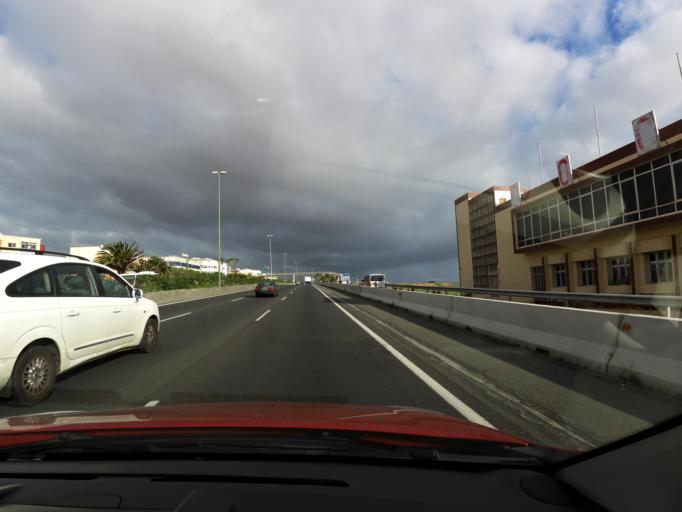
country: ES
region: Canary Islands
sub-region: Provincia de Las Palmas
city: Telde
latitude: 27.9832
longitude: -15.3919
